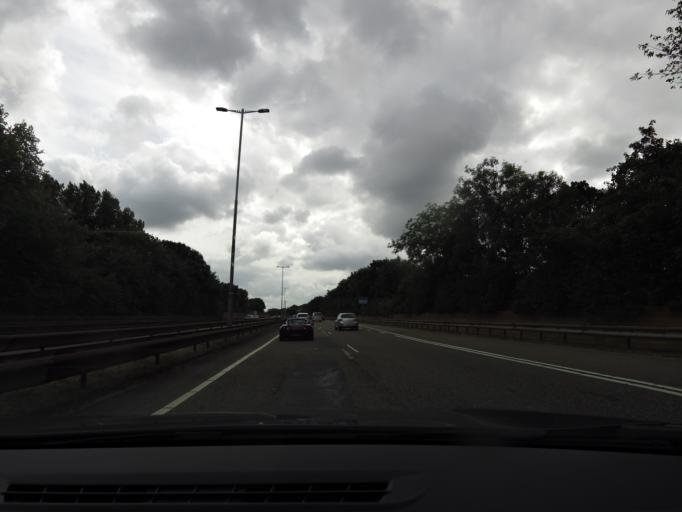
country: NL
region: Utrecht
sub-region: Gemeente Utrecht
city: Lunetten
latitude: 52.0705
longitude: 5.1317
